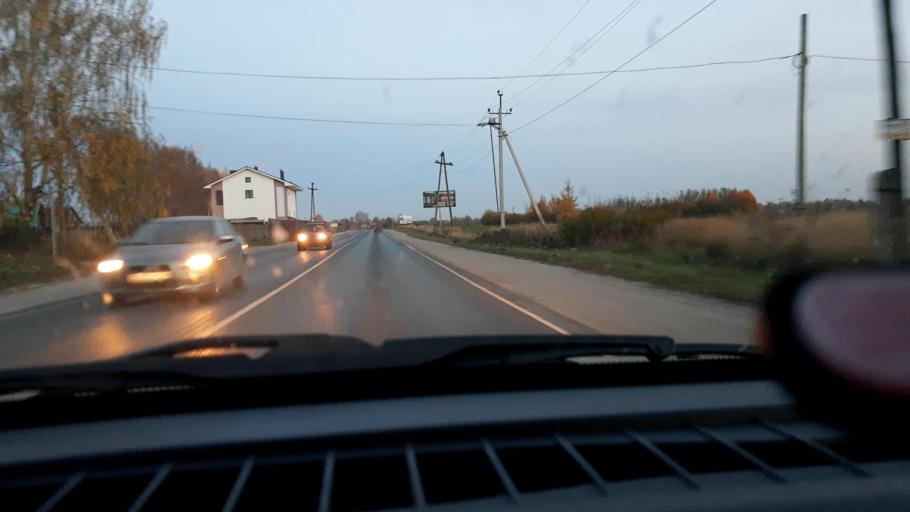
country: RU
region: Nizjnij Novgorod
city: Gorodets
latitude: 56.6397
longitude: 43.5043
